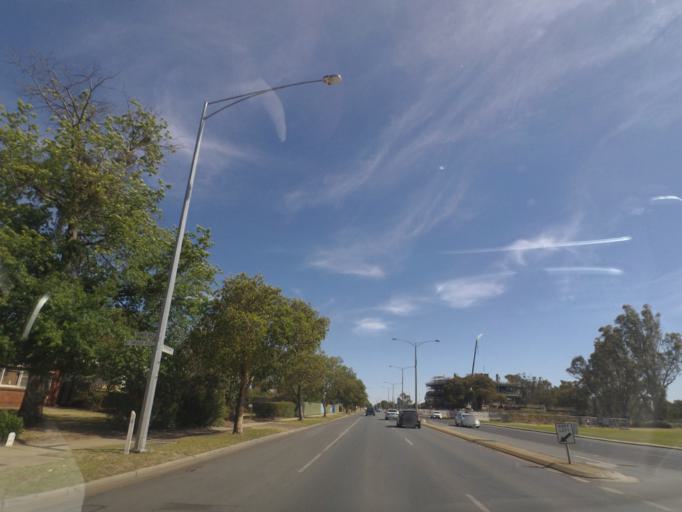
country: AU
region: Victoria
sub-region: Greater Shepparton
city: Shepparton
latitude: -36.3894
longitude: 145.3977
